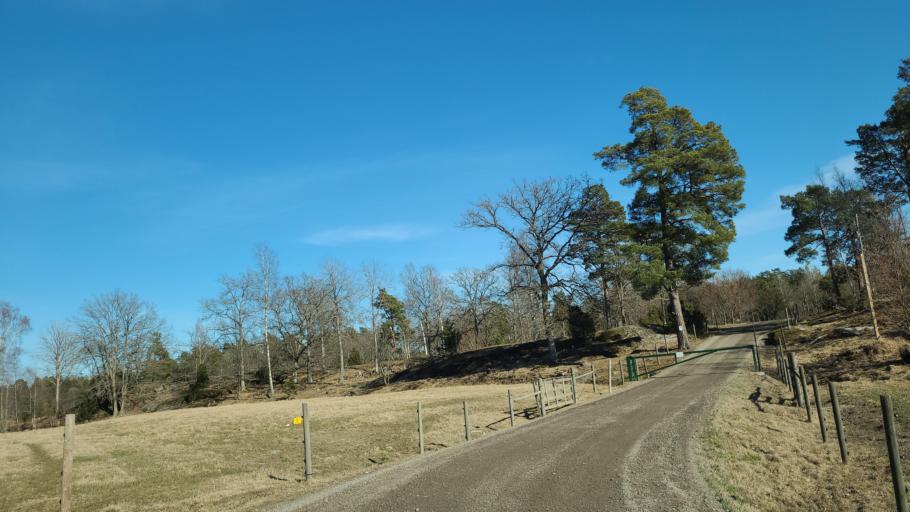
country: SE
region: Stockholm
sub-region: Varmdo Kommun
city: Holo
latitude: 59.2800
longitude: 18.6138
